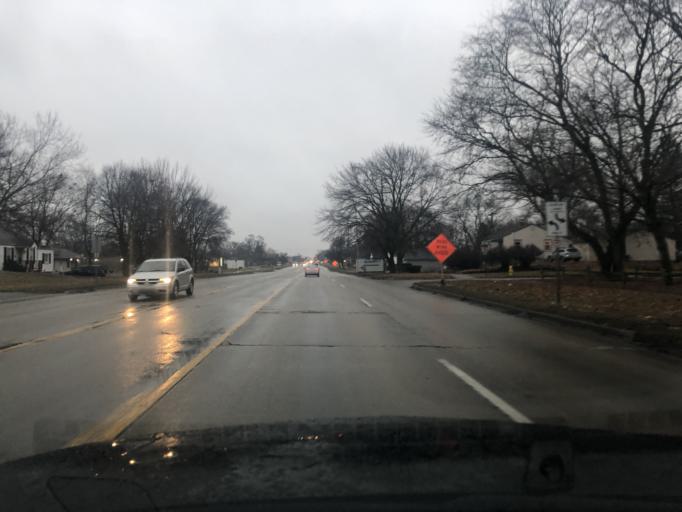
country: US
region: Michigan
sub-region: Wayne County
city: Garden City
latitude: 42.3032
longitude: -83.3496
